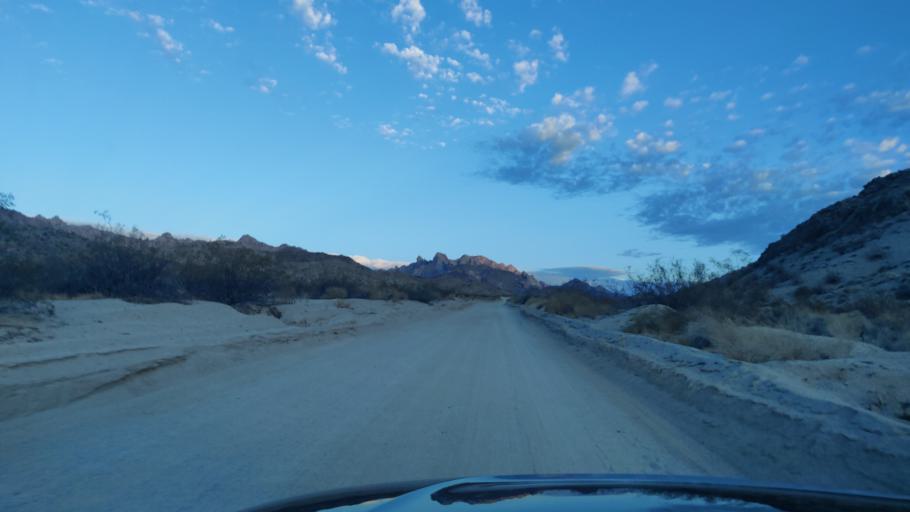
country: US
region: Nevada
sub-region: Clark County
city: Laughlin
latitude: 35.2035
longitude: -114.6699
